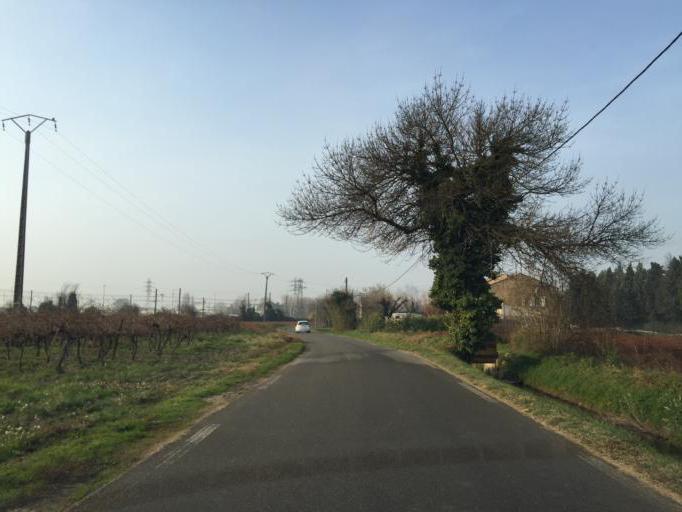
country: FR
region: Provence-Alpes-Cote d'Azur
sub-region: Departement du Vaucluse
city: Orange
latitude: 44.1330
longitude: 4.8458
